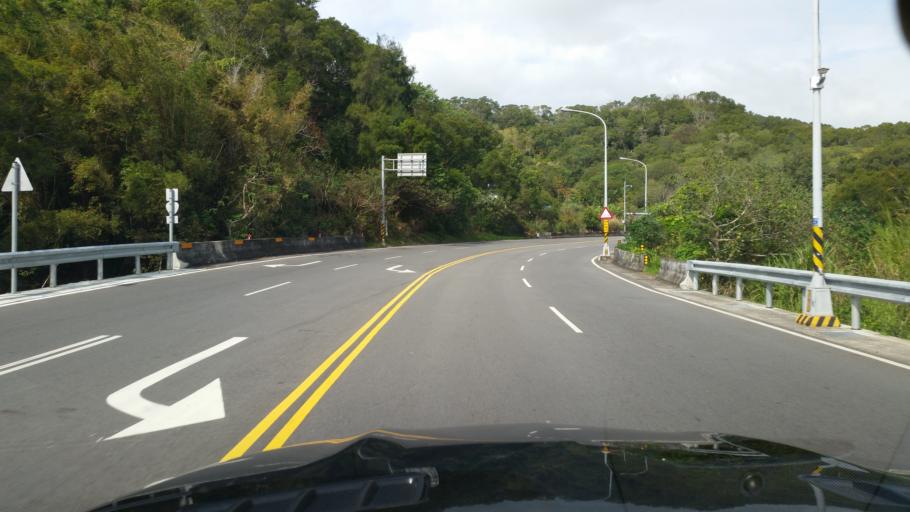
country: TW
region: Taiwan
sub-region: Miaoli
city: Miaoli
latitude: 24.6339
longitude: 120.8579
